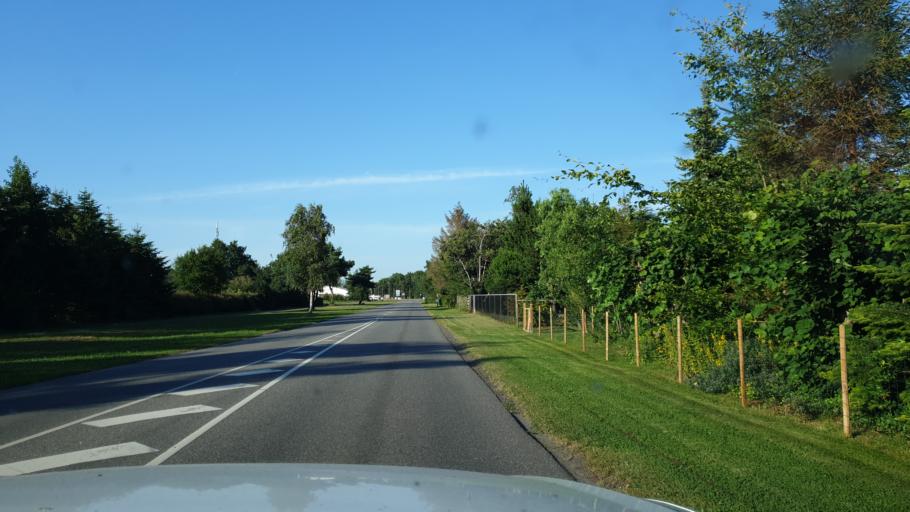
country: DK
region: Zealand
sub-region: Guldborgsund Kommune
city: Nykobing Falster
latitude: 54.7014
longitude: 11.9634
